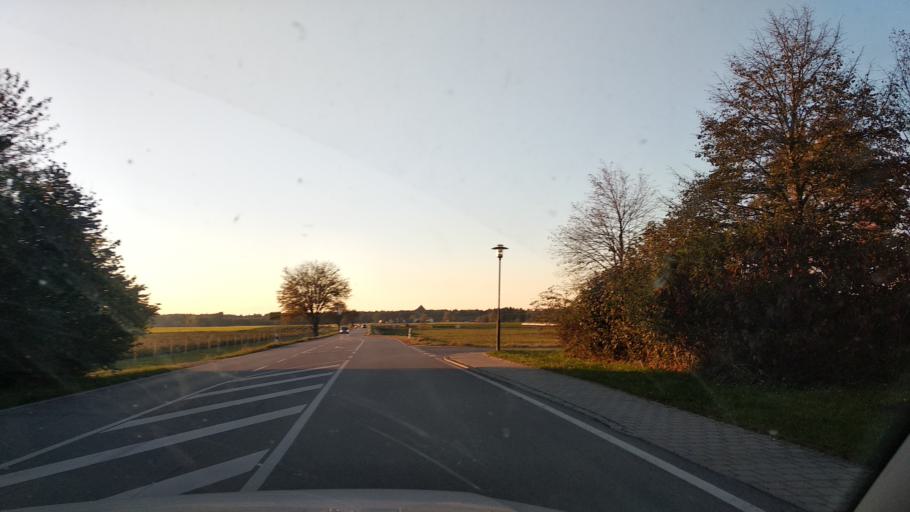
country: DE
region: Bavaria
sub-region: Upper Bavaria
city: Egmating
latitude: 48.0082
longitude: 11.7885
